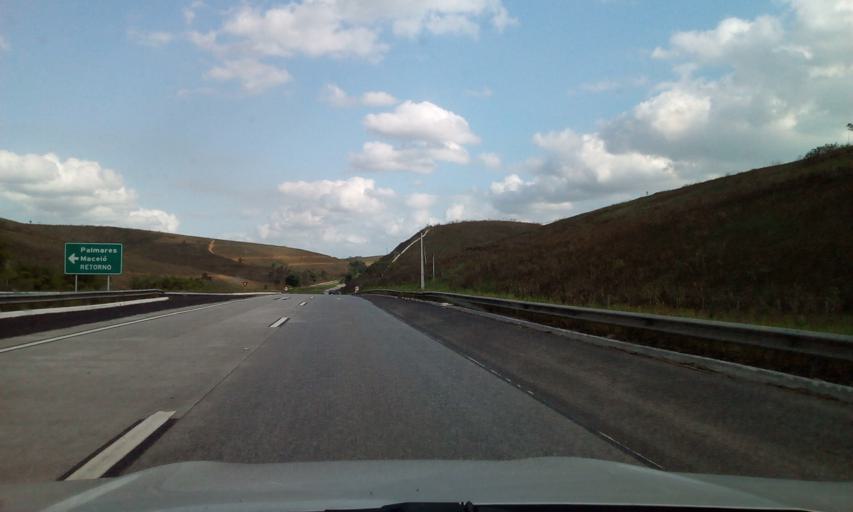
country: BR
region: Pernambuco
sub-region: Gameleira
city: Gameleira
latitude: -8.5533
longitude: -35.4357
